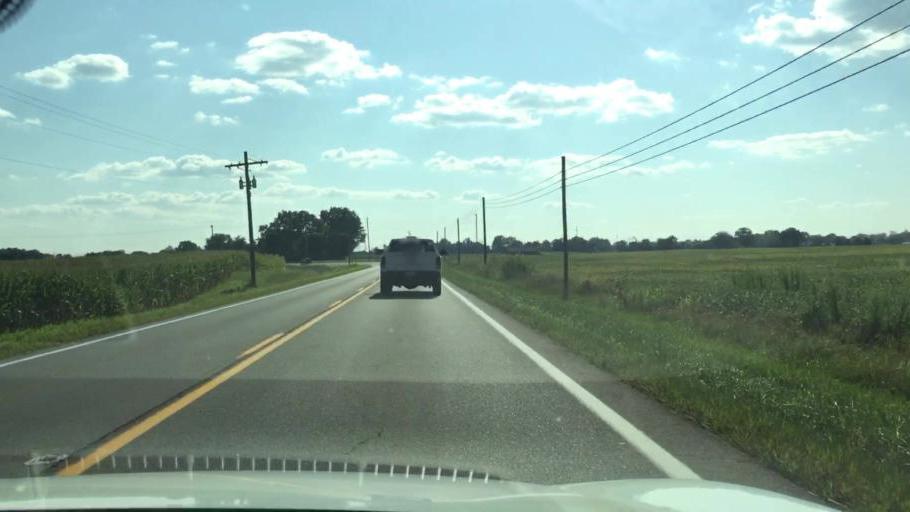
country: US
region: Ohio
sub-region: Champaign County
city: Mechanicsburg
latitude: 40.1155
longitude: -83.5149
